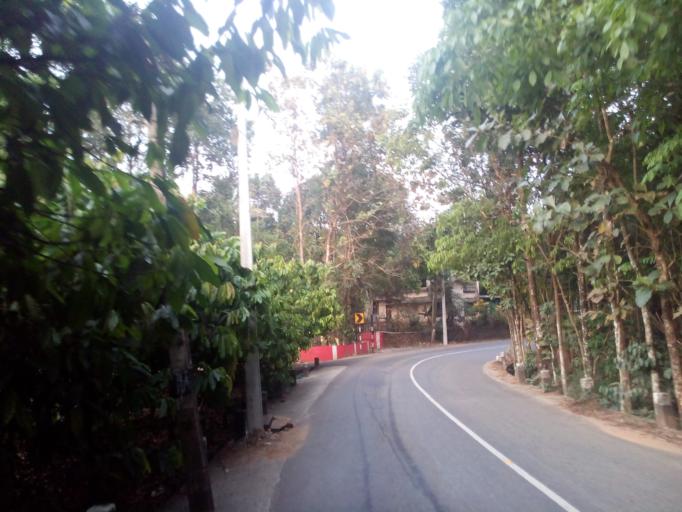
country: IN
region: Kerala
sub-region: Kottayam
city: Palackattumala
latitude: 9.8226
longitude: 76.6686
